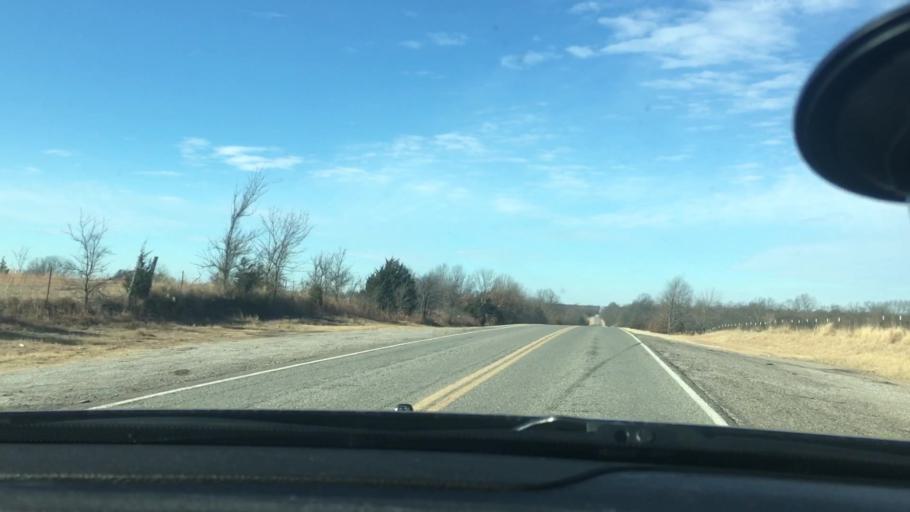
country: US
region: Oklahoma
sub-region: Seminole County
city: Konawa
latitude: 34.9856
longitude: -96.8411
